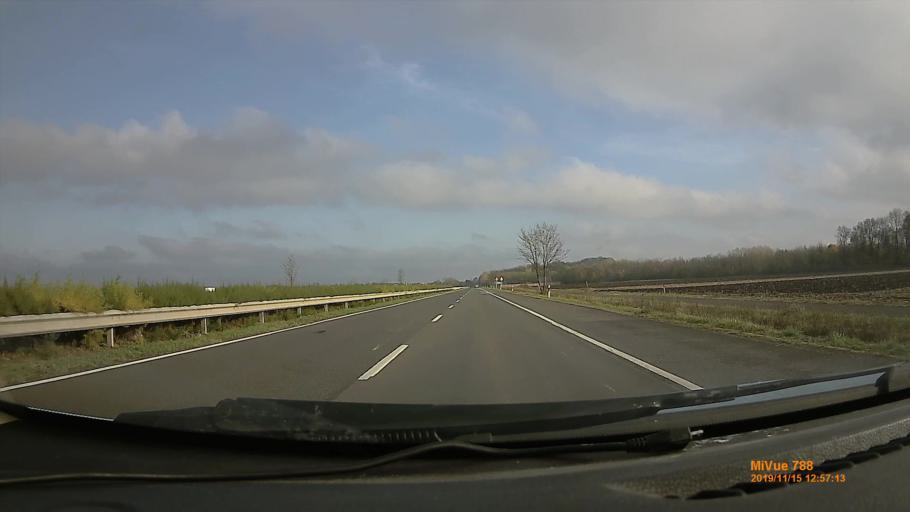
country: HU
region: Bekes
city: Bekescsaba
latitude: 46.6740
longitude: 21.1587
